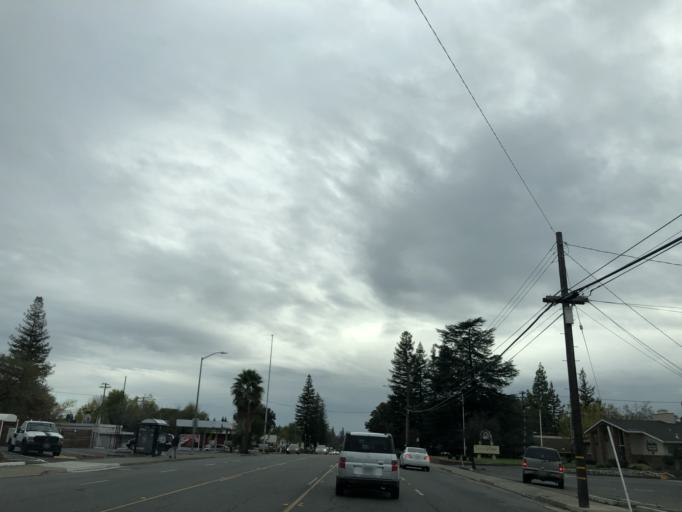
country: US
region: California
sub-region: Sacramento County
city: Carmichael
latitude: 38.6146
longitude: -121.3288
